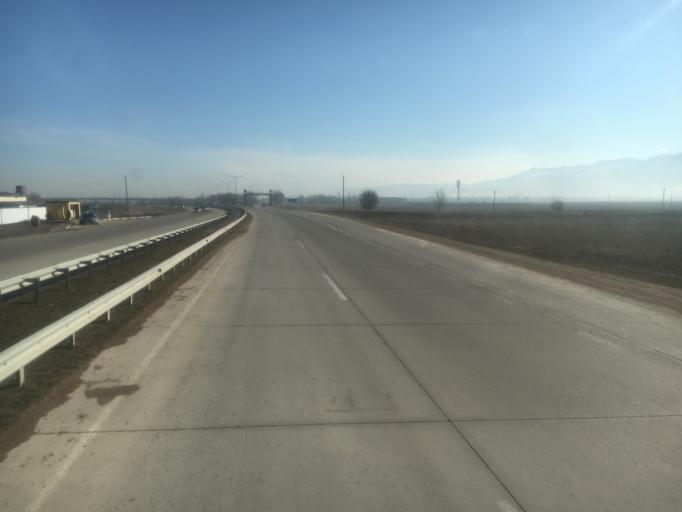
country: KZ
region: Zhambyl
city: Merke
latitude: 42.8747
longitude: 73.1269
